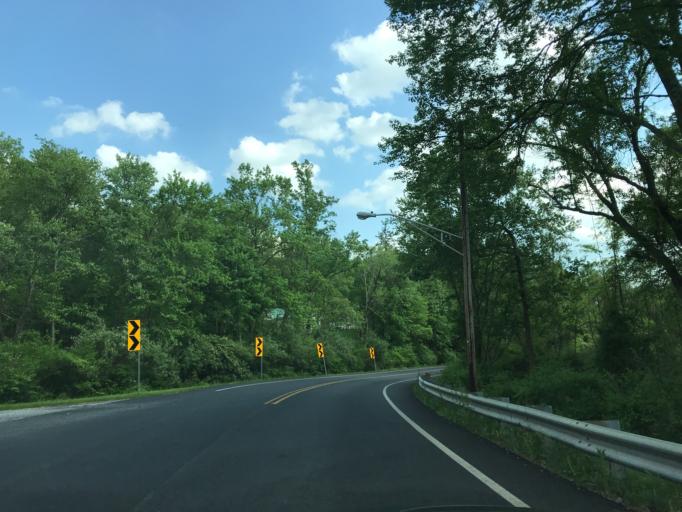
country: US
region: Maryland
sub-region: Harford County
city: Bel Air North
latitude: 39.5450
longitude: -76.3925
